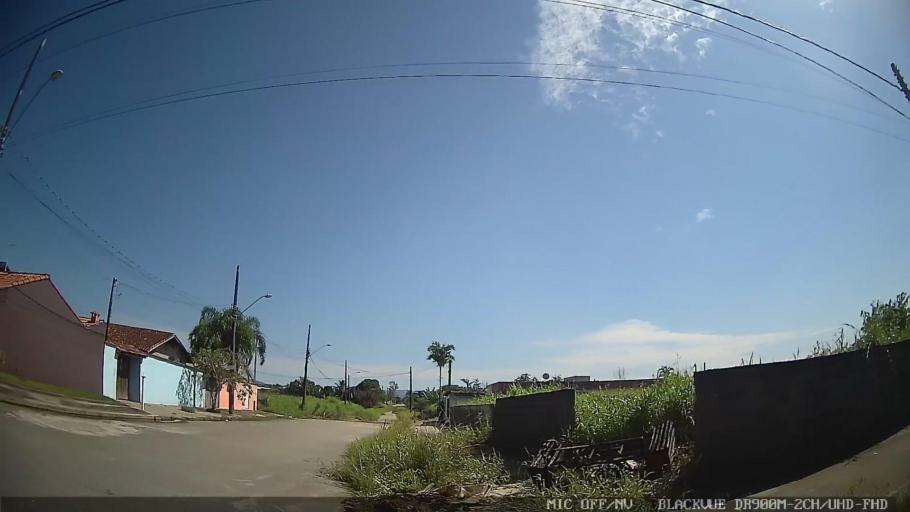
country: BR
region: Sao Paulo
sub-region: Itanhaem
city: Itanhaem
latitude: -24.2109
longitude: -46.8507
